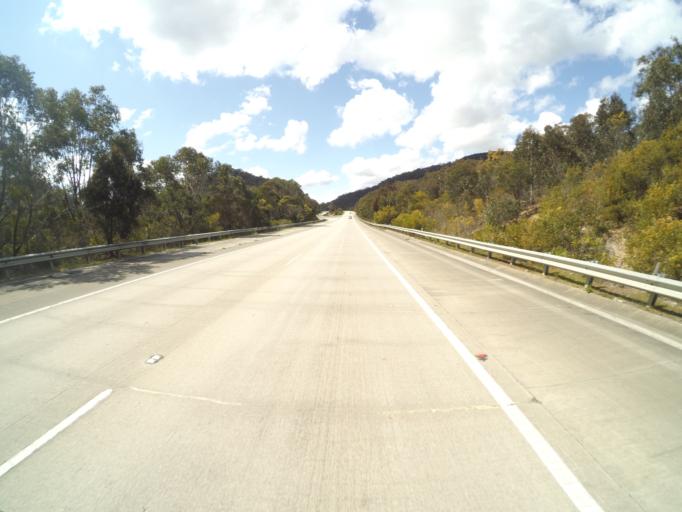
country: AU
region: New South Wales
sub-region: Wingecarribee
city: Mittagong
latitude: -34.4325
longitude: 150.4515
